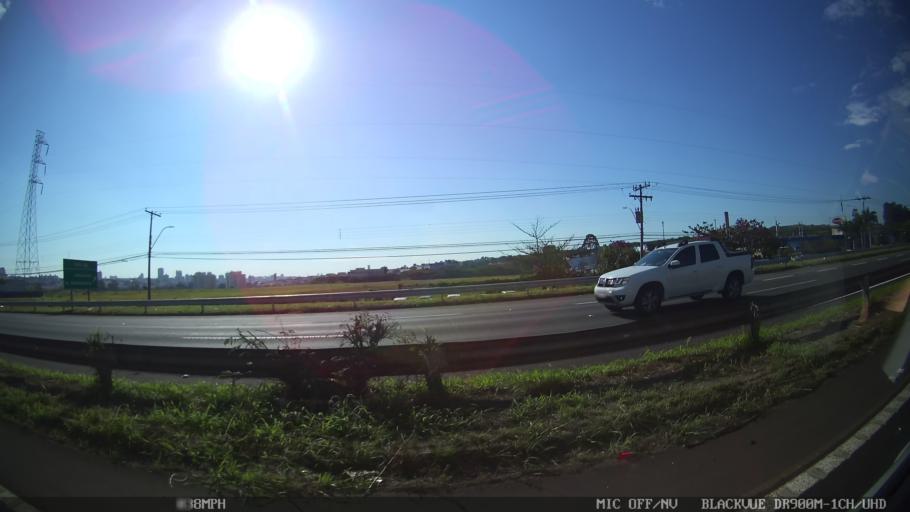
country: BR
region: Sao Paulo
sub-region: Nova Odessa
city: Nova Odessa
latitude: -22.7571
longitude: -47.3119
